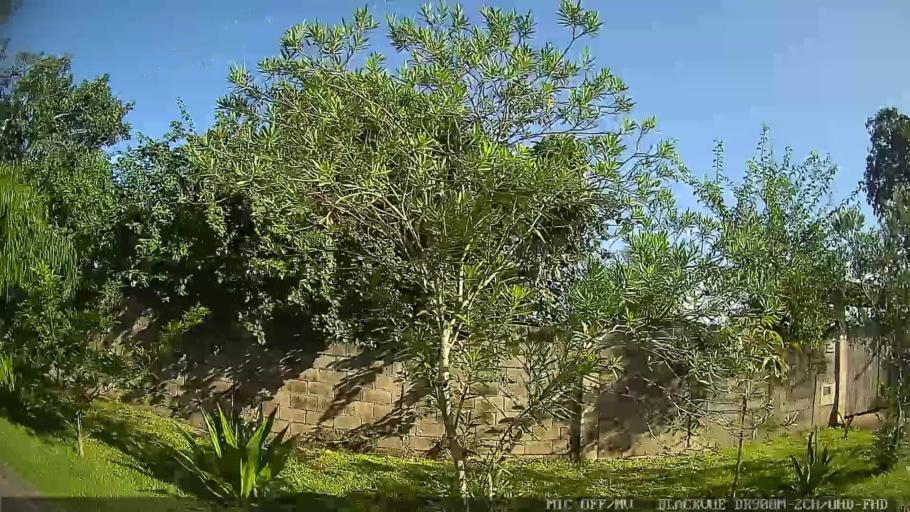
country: BR
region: Sao Paulo
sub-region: Peruibe
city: Peruibe
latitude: -24.2726
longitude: -46.9493
